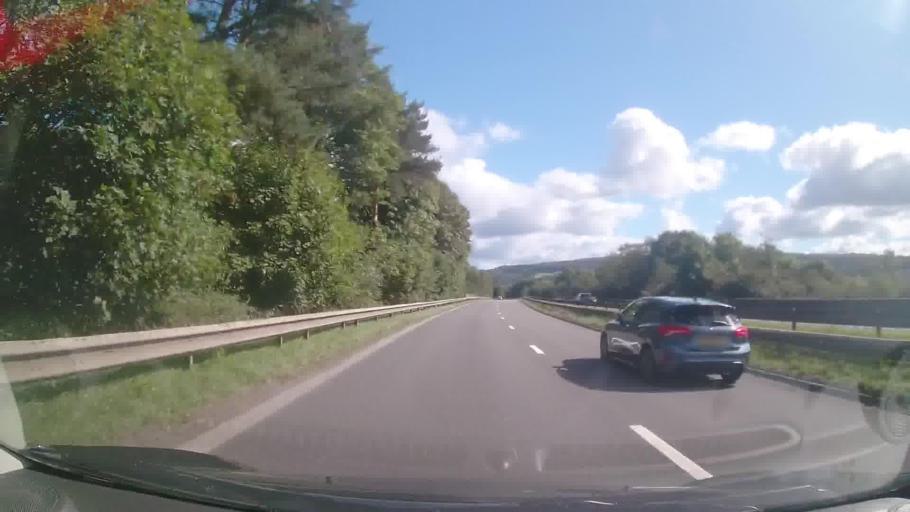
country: GB
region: Wales
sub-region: Neath Port Talbot
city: Neath
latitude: 51.6680
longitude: -3.8055
